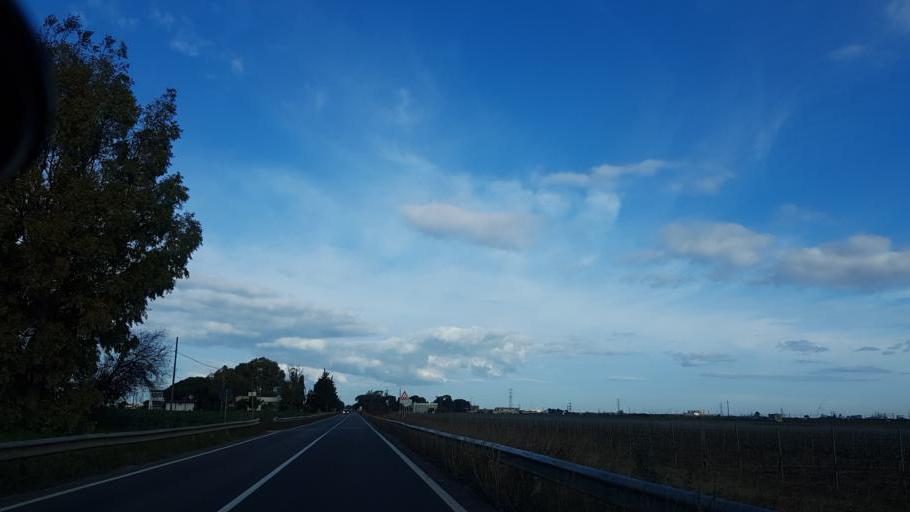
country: IT
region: Apulia
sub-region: Provincia di Brindisi
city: La Rosa
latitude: 40.5794
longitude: 17.9650
